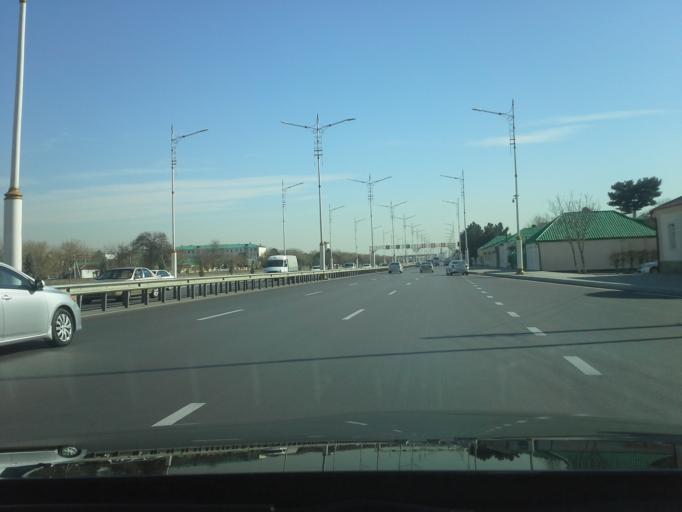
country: TM
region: Ahal
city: Ashgabat
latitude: 37.9540
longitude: 58.3751
